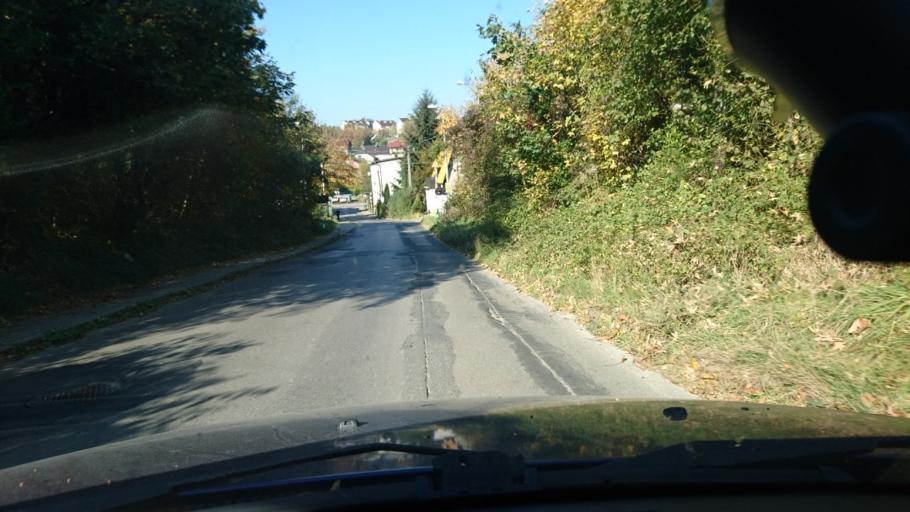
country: PL
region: Silesian Voivodeship
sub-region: Bielsko-Biala
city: Bielsko-Biala
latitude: 49.8292
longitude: 19.0329
